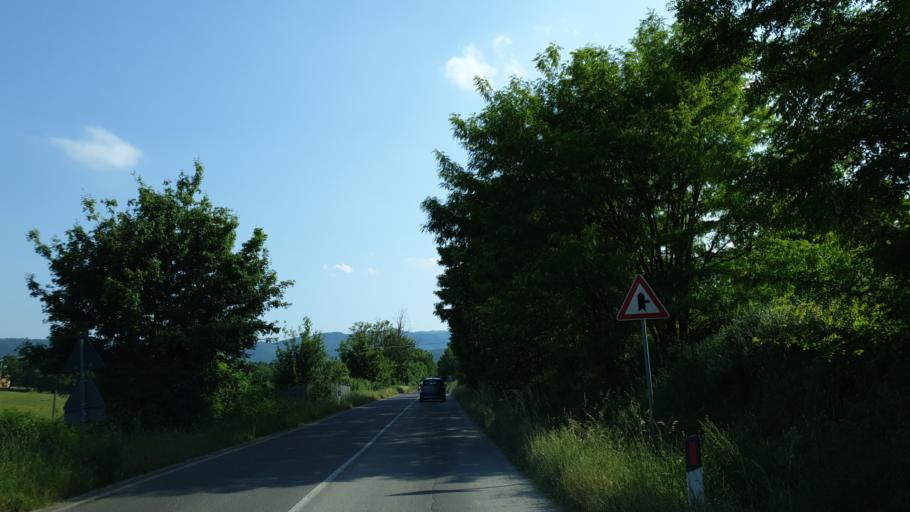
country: IT
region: Tuscany
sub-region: Province of Arezzo
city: Soci
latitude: 43.7353
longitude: 11.7922
